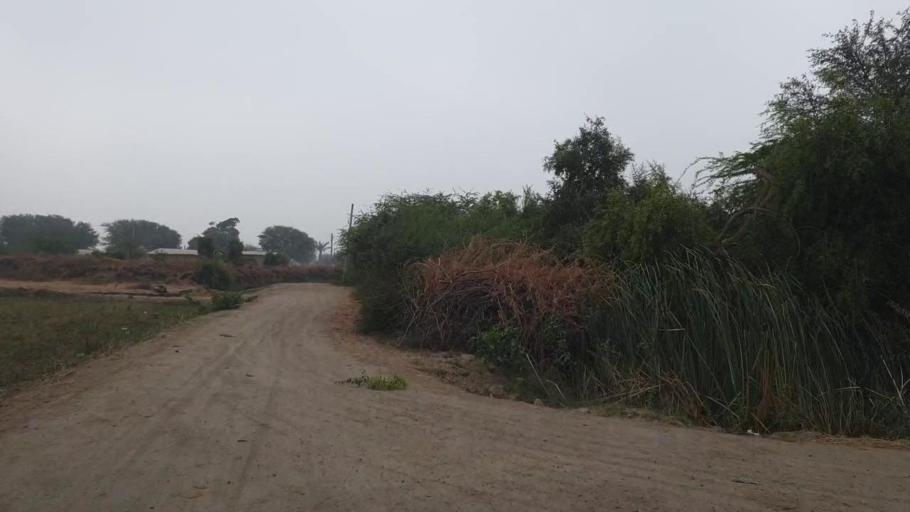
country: PK
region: Sindh
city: Badin
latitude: 24.5693
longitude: 68.6516
